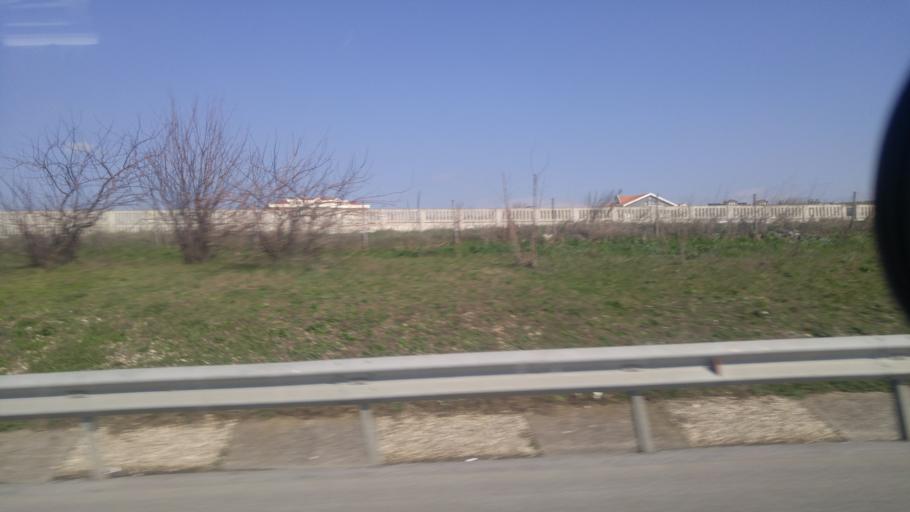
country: TR
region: Istanbul
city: Selimpasa
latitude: 41.0753
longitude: 28.3765
